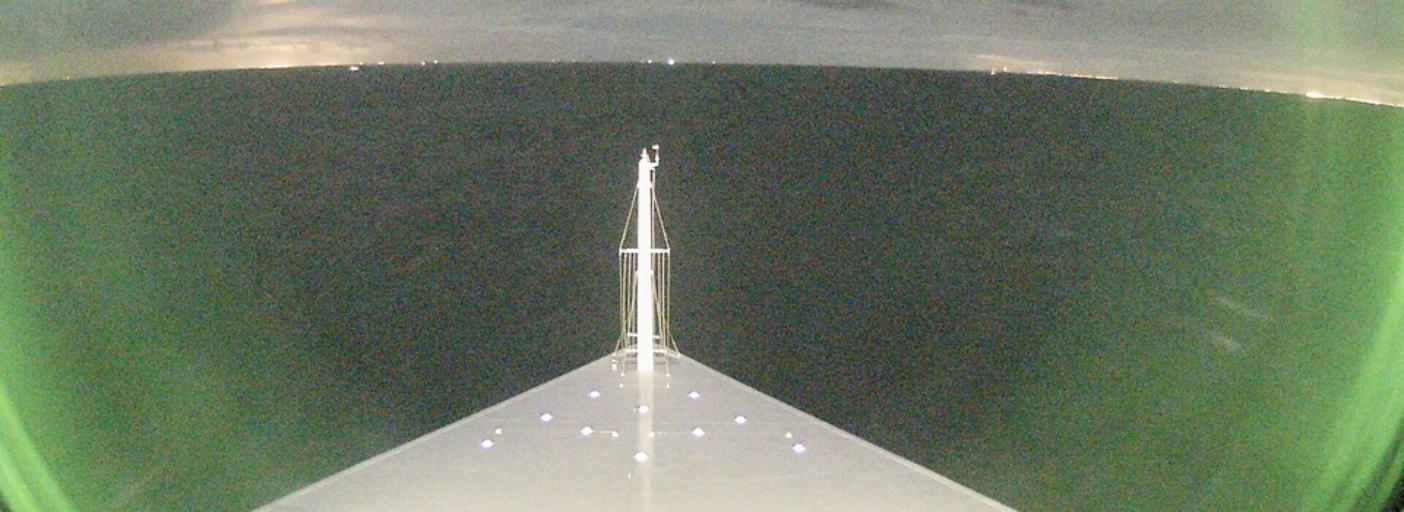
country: FR
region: Nord-Pas-de-Calais
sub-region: Departement du Pas-de-Calais
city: Calais
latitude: 51.3153
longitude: 1.8356
